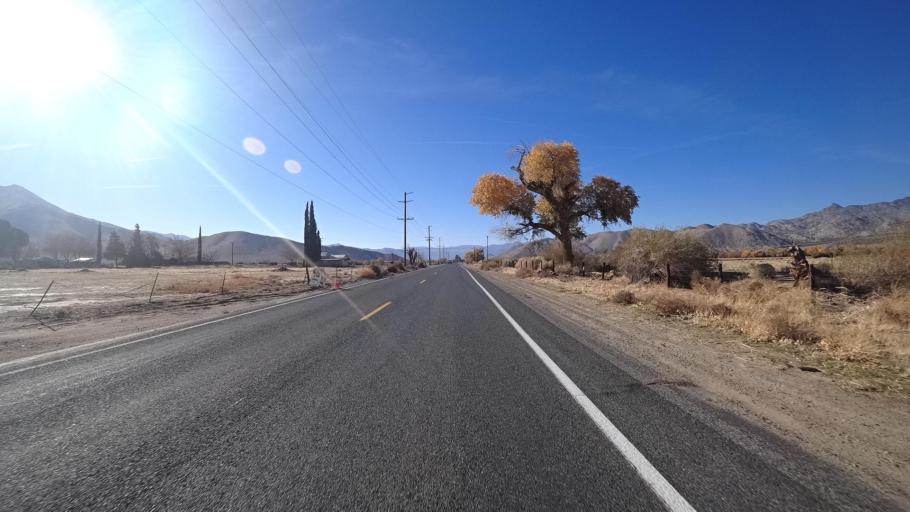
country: US
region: California
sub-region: Kern County
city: Weldon
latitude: 35.6672
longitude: -118.2706
